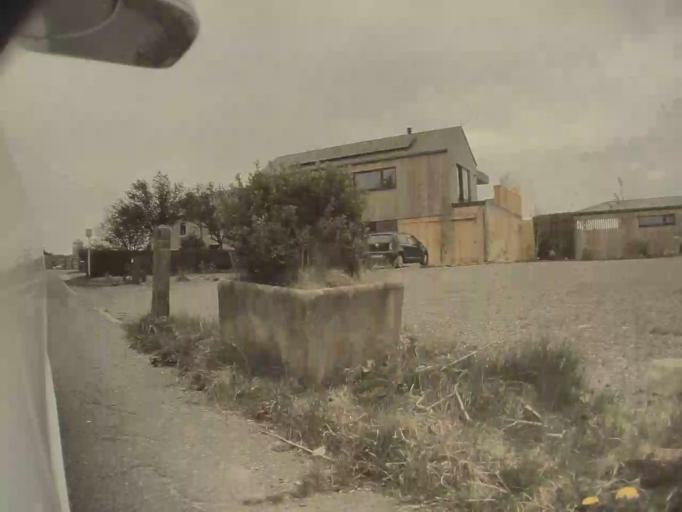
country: BE
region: Wallonia
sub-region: Province du Luxembourg
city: La Roche-en-Ardenne
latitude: 50.2324
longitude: 5.6174
